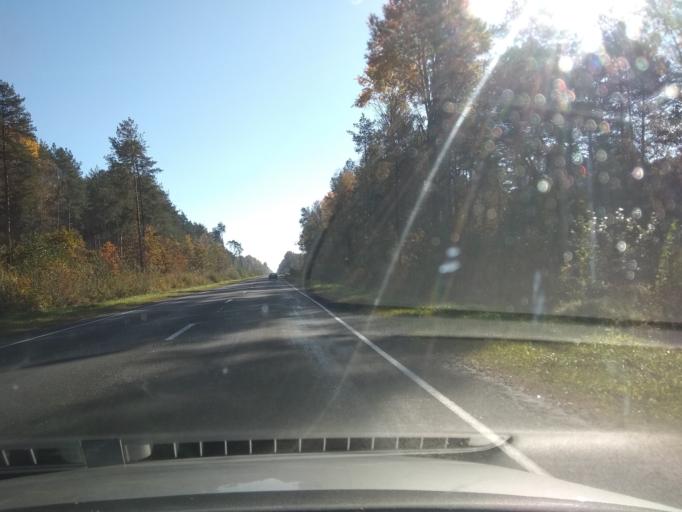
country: BY
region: Brest
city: Malaryta
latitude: 51.9100
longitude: 24.1040
